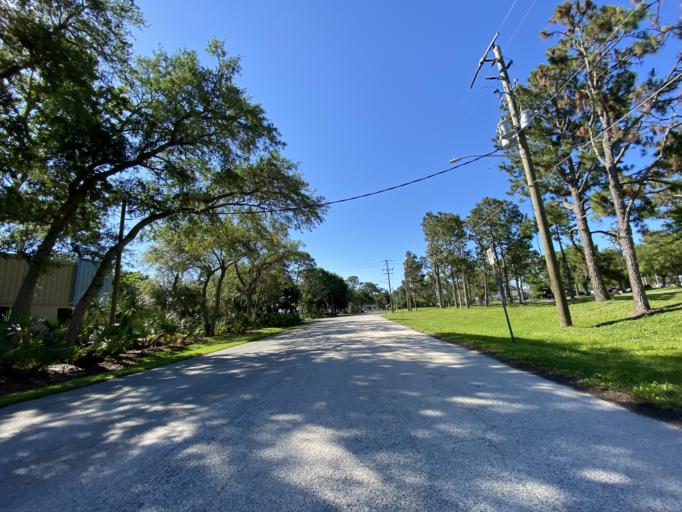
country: US
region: Florida
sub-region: Volusia County
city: Port Orange
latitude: 29.1534
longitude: -80.9950
